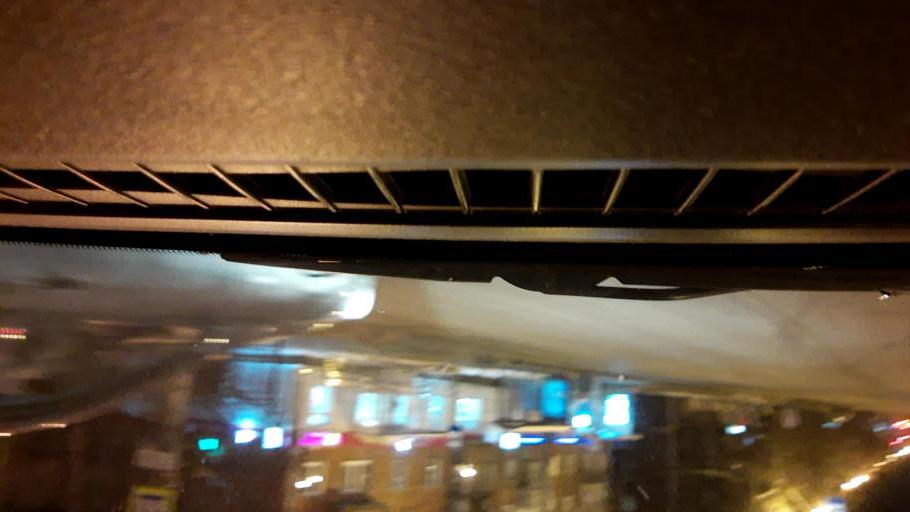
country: RU
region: Nizjnij Novgorod
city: Nizhniy Novgorod
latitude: 56.2907
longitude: 44.0173
